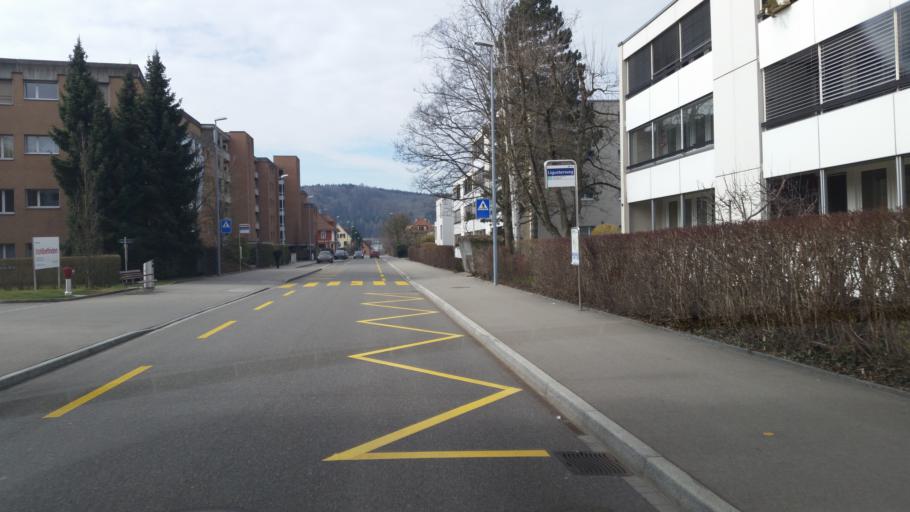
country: CH
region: Aargau
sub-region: Bezirk Baden
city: Neuenhof
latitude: 47.4607
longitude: 8.3223
